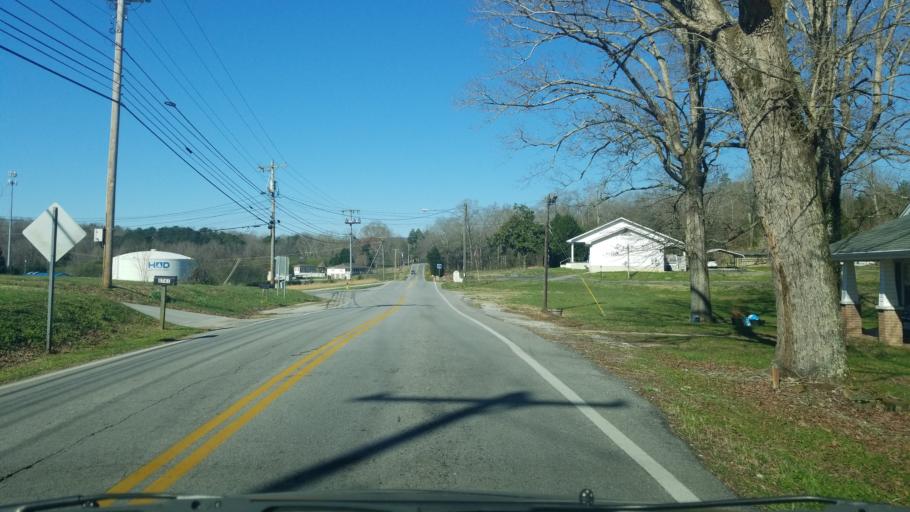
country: US
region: Tennessee
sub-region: Hamilton County
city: Middle Valley
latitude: 35.2151
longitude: -85.1807
